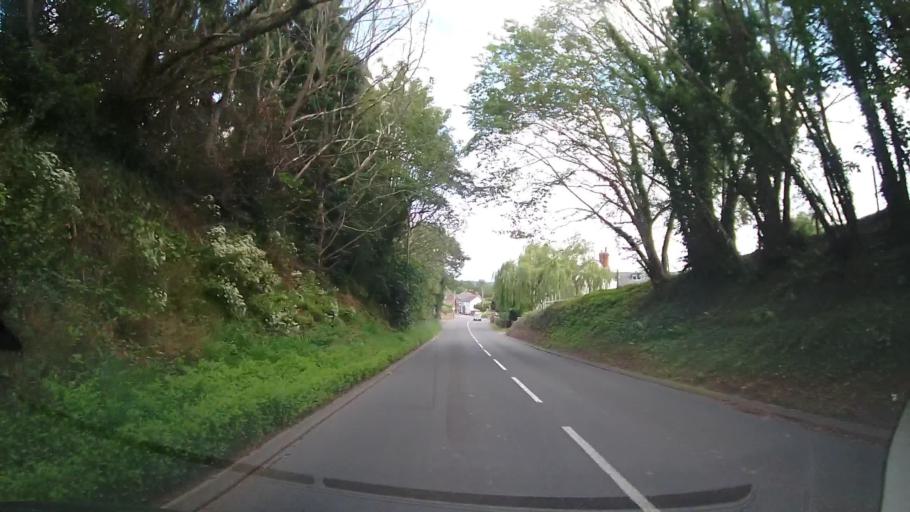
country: GB
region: England
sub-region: Shropshire
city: Whittington
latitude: 52.7947
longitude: -2.9953
